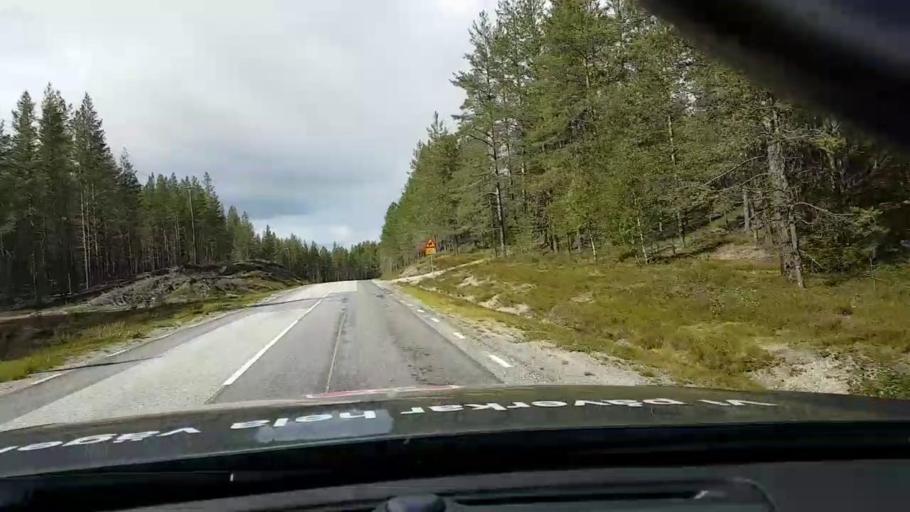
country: SE
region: Vaesterbotten
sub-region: Asele Kommun
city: Asele
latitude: 63.8551
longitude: 17.3883
